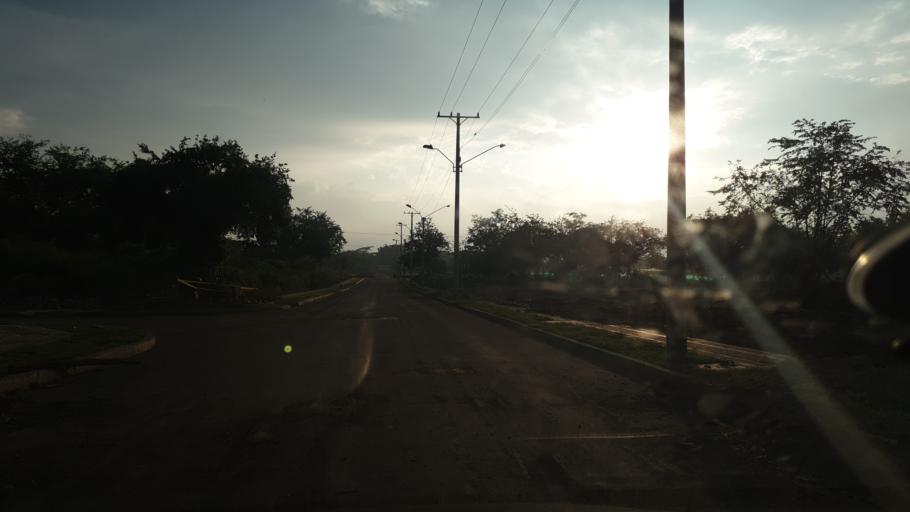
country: CO
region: Valle del Cauca
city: Jamundi
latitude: 3.3449
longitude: -76.5193
